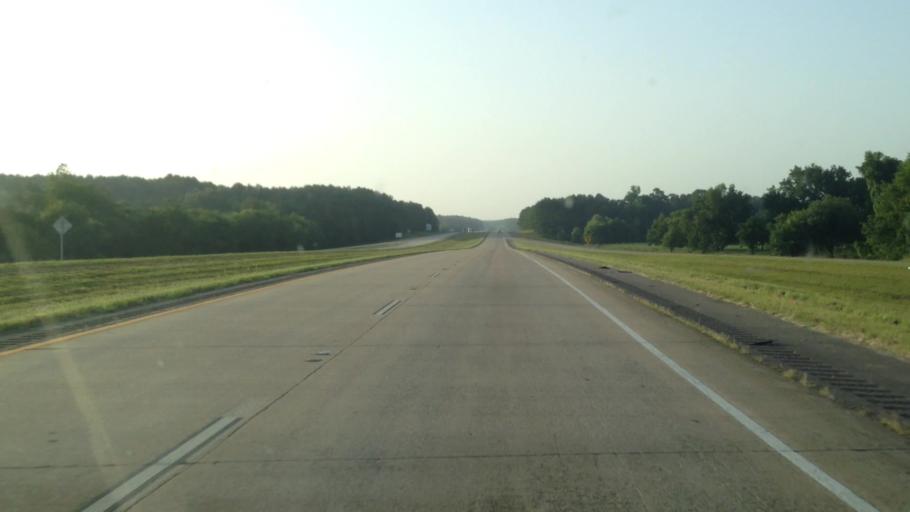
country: US
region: Louisiana
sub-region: Grant Parish
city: Colfax
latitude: 31.4935
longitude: -92.8604
